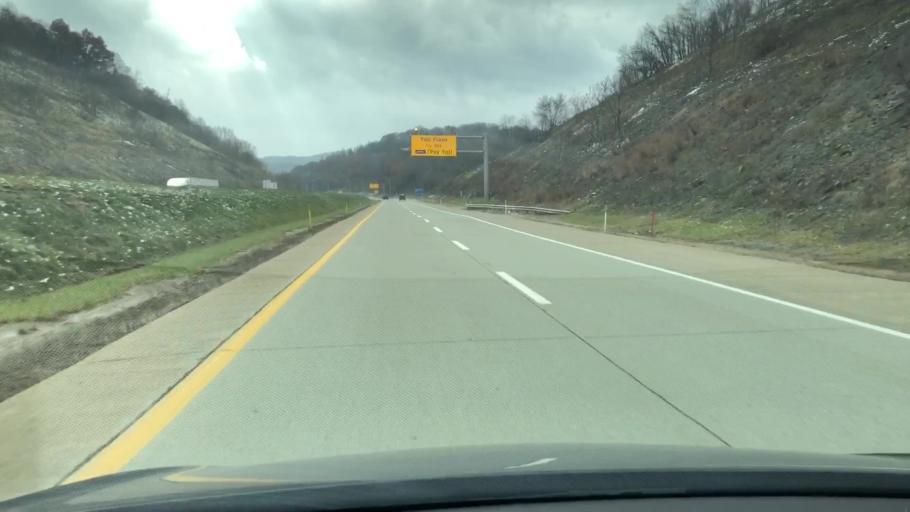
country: US
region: Pennsylvania
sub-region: Westmoreland County
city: Jeannette
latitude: 40.2973
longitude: -79.6089
